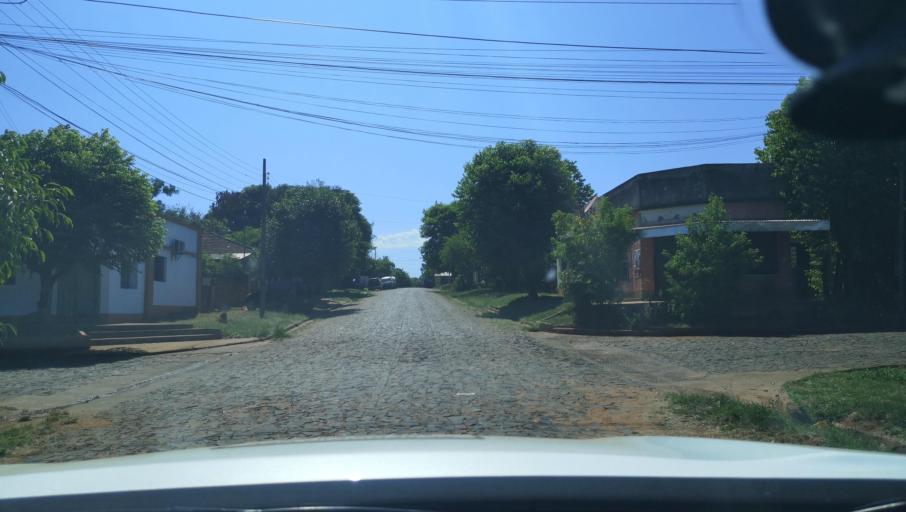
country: PY
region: Itapua
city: Carmen del Parana
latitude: -27.1588
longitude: -56.2346
